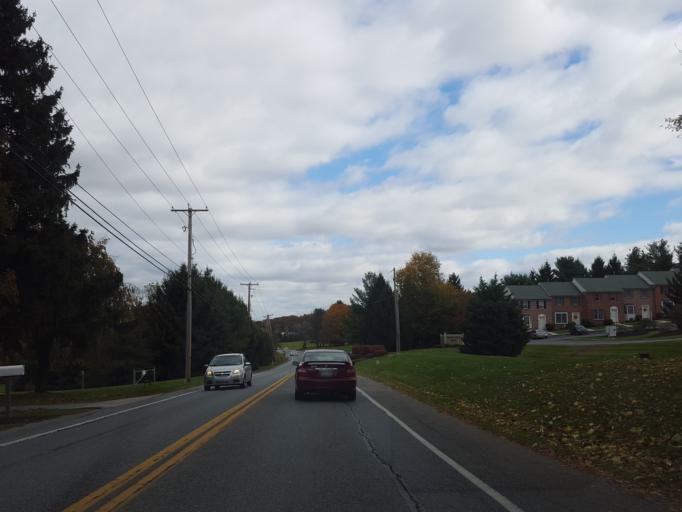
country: US
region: Pennsylvania
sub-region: York County
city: Yoe
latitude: 39.9177
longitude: -76.6245
